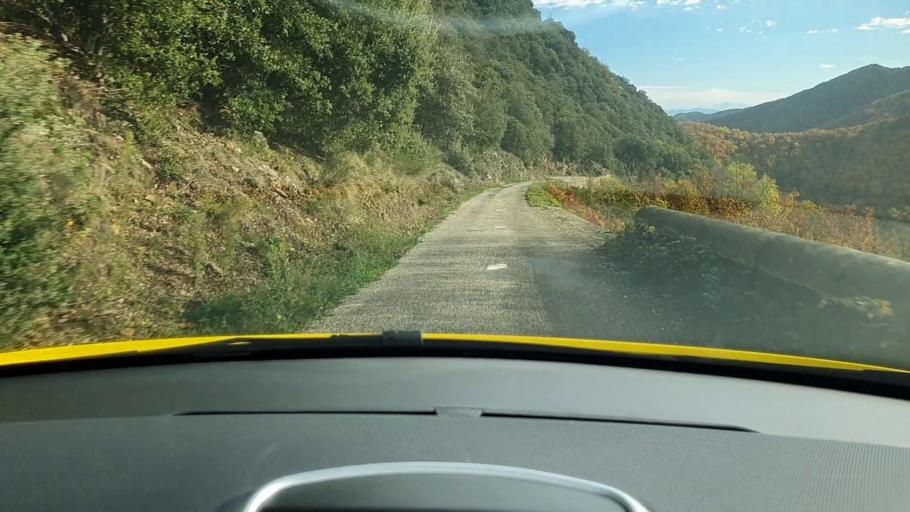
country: FR
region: Languedoc-Roussillon
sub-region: Departement du Gard
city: Valleraugue
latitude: 44.0842
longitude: 3.7342
